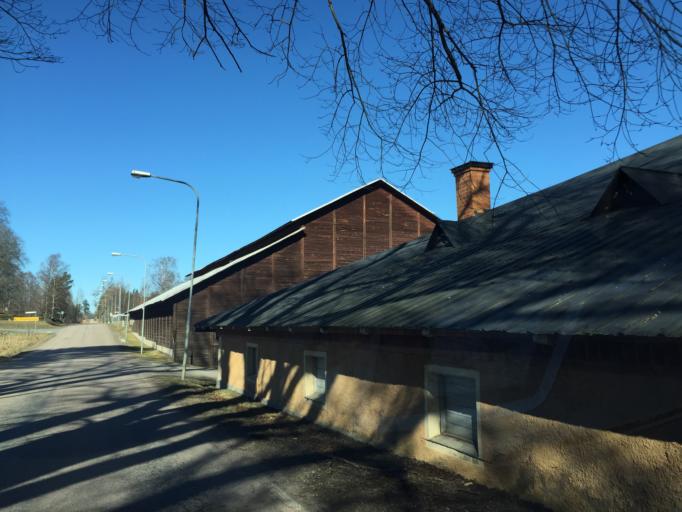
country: SE
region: OErebro
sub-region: Orebro Kommun
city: Odensbacken
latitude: 59.0138
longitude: 15.5797
